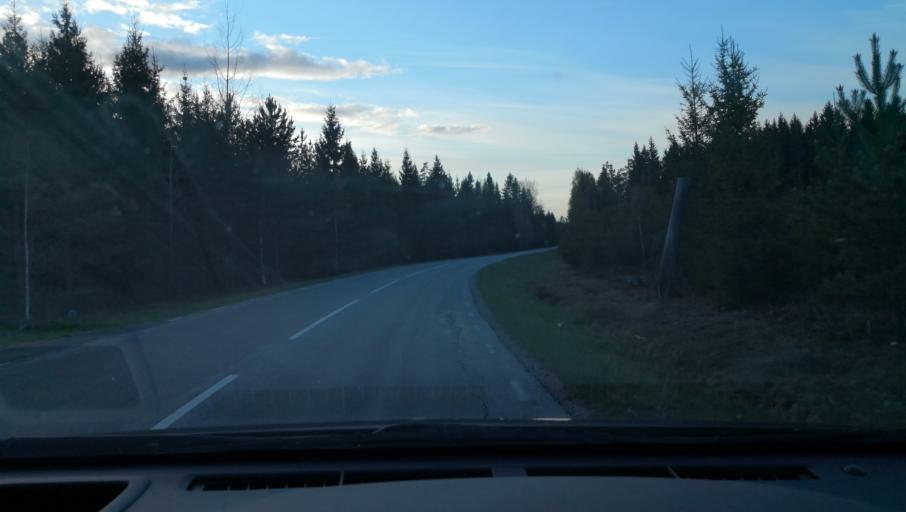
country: SE
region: OErebro
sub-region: Askersunds Kommun
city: Asbro
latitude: 58.9013
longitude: 15.1027
